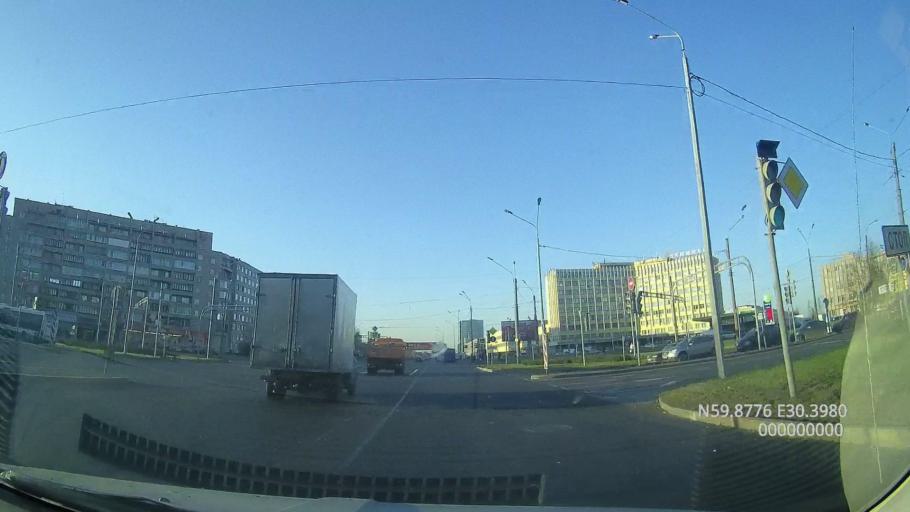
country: RU
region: St.-Petersburg
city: Kupchino
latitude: 59.8776
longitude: 30.3977
